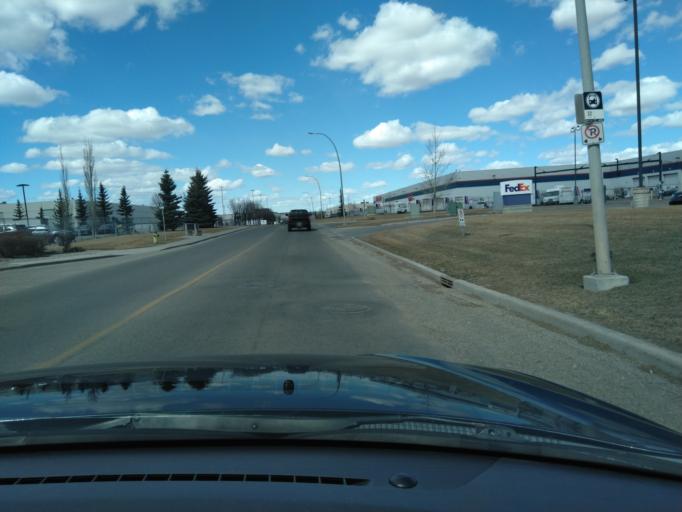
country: CA
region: Alberta
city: Calgary
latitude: 51.1192
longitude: -114.0329
